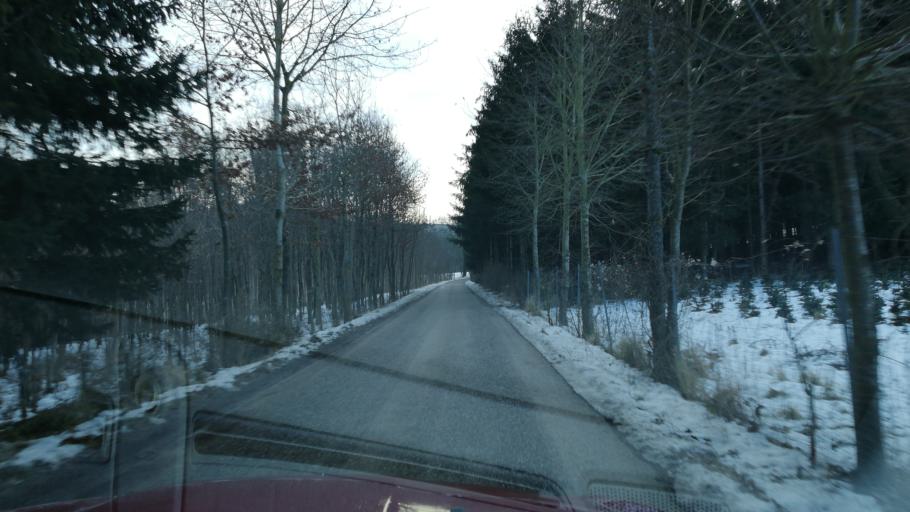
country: AT
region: Upper Austria
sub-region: Wels-Land
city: Buchkirchen
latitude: 48.2385
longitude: 13.9864
